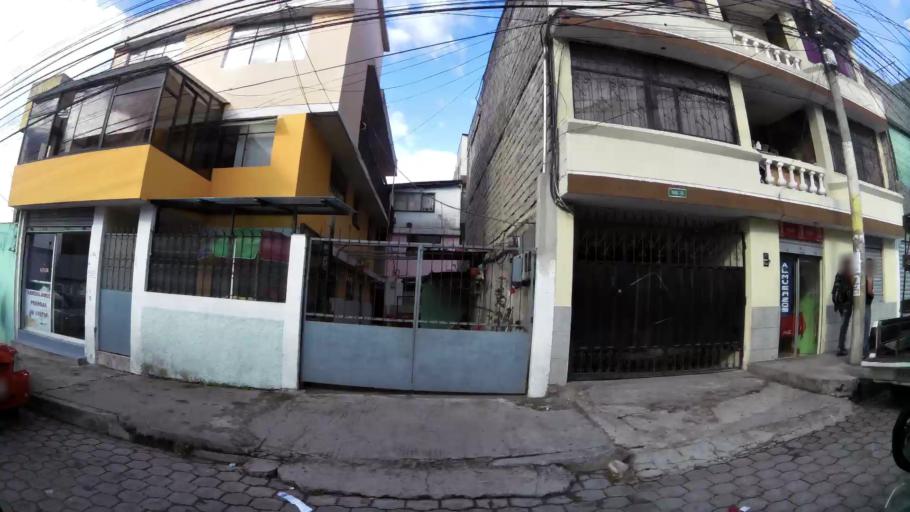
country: EC
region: Pichincha
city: Quito
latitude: -0.1294
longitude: -78.4705
